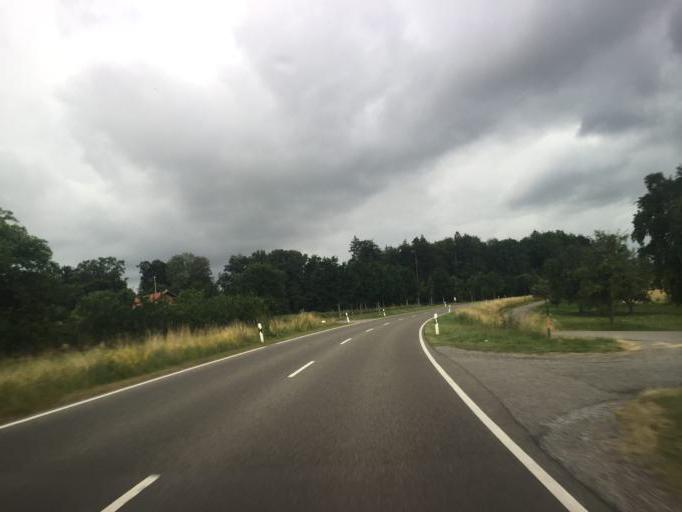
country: DE
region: Baden-Wuerttemberg
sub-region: Regierungsbezirk Stuttgart
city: Nufringen
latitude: 48.6442
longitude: 8.8692
